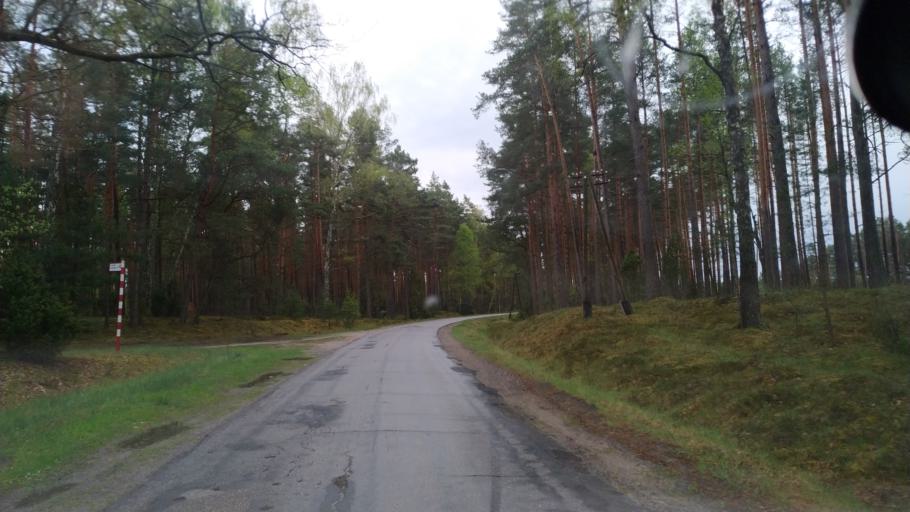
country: PL
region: Pomeranian Voivodeship
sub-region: Powiat starogardzki
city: Osiek
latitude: 53.6548
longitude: 18.4898
